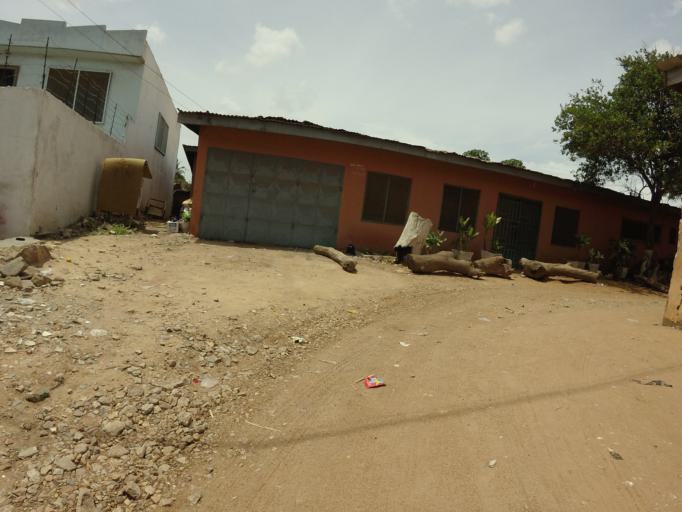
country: GH
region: Greater Accra
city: Dome
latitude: 5.6104
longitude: -0.2448
